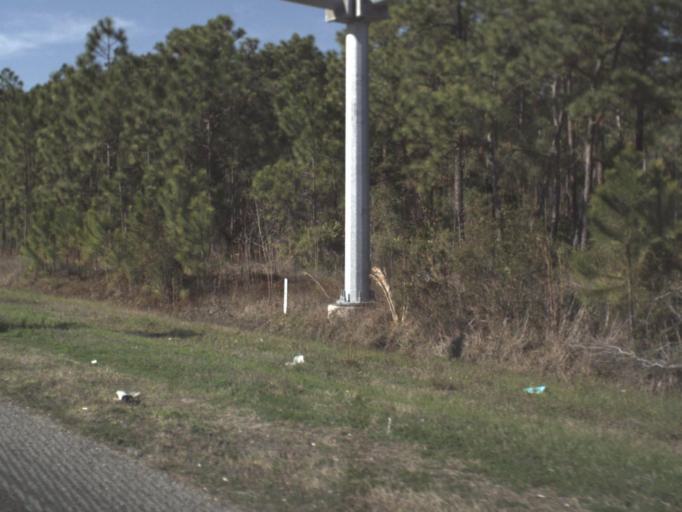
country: US
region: Florida
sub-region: Bay County
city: Panama City Beach
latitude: 30.1908
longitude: -85.7927
